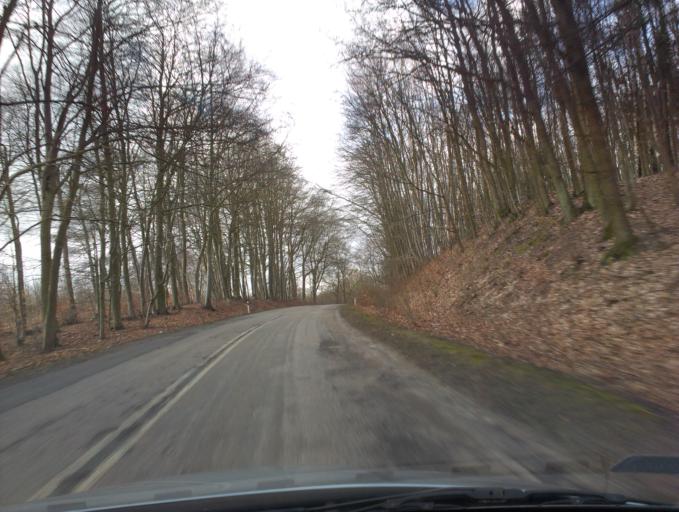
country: PL
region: Pomeranian Voivodeship
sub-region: Powiat czluchowski
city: Rzeczenica
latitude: 53.6729
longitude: 17.0877
